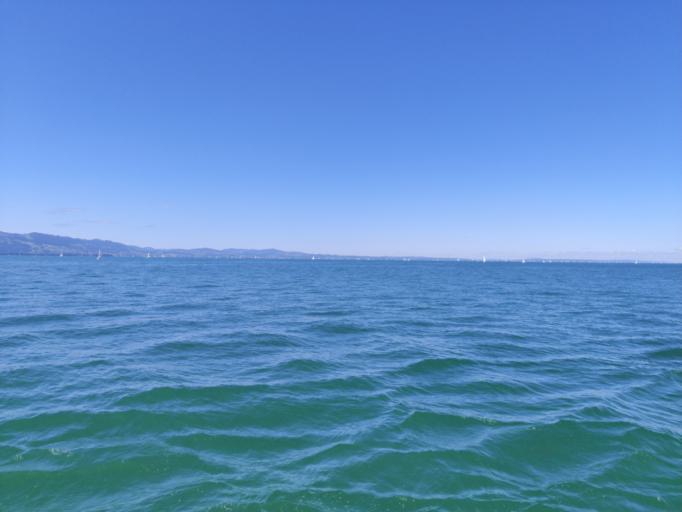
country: DE
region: Bavaria
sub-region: Swabia
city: Bodolz
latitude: 47.5507
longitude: 9.6456
